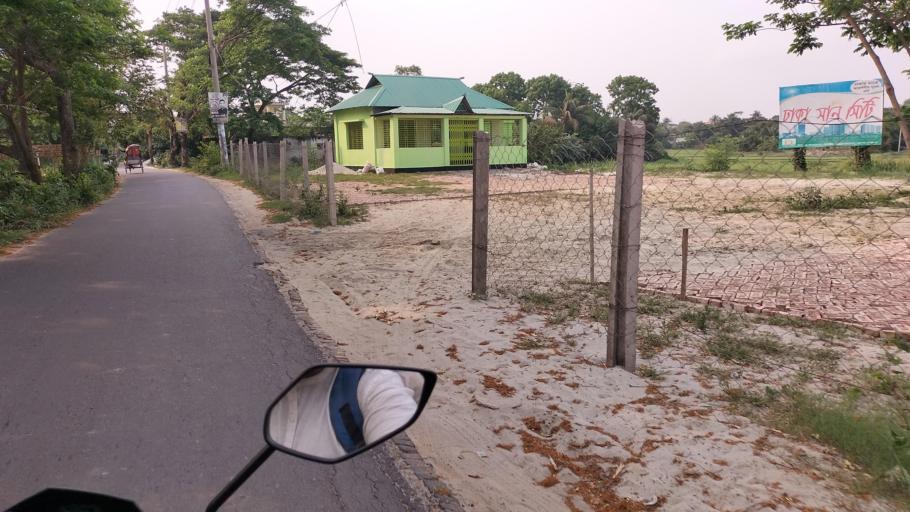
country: BD
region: Dhaka
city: Azimpur
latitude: 23.6690
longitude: 90.3466
